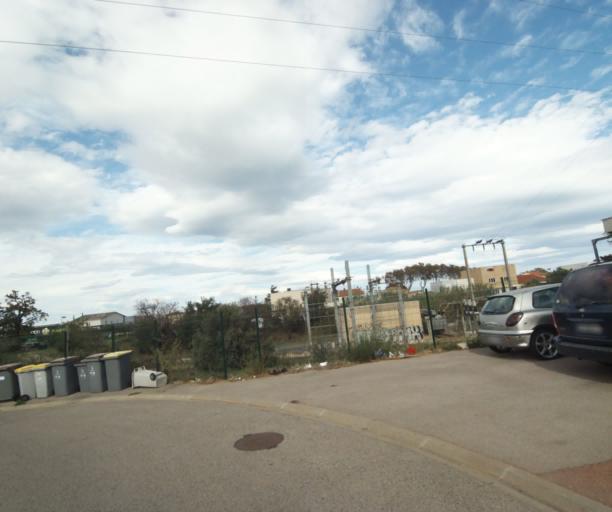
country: FR
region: Languedoc-Roussillon
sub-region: Departement des Pyrenees-Orientales
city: Argelers
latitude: 42.5492
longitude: 3.0119
